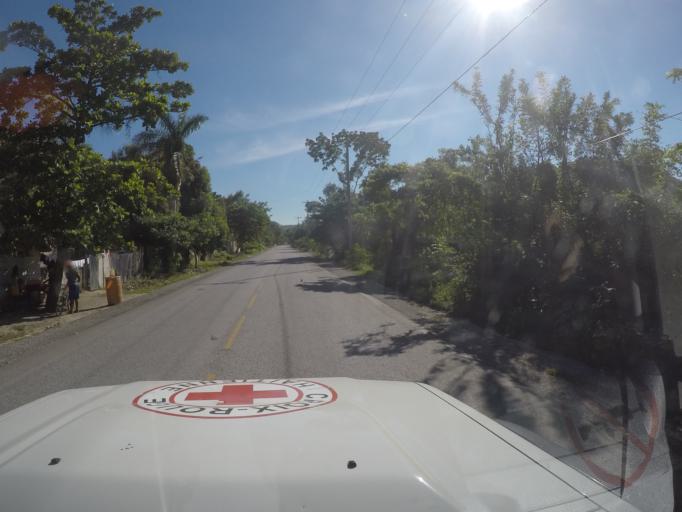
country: HT
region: Ouest
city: Leogane
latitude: 18.4518
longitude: -72.6408
